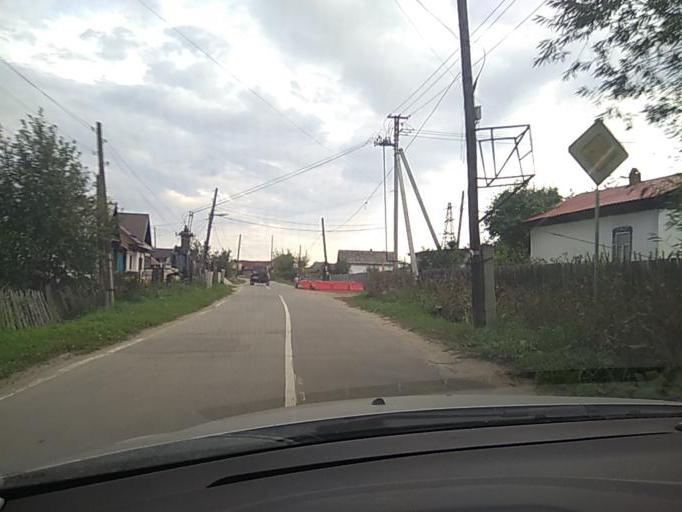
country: RU
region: Chelyabinsk
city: Kyshtym
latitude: 55.6953
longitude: 60.5313
